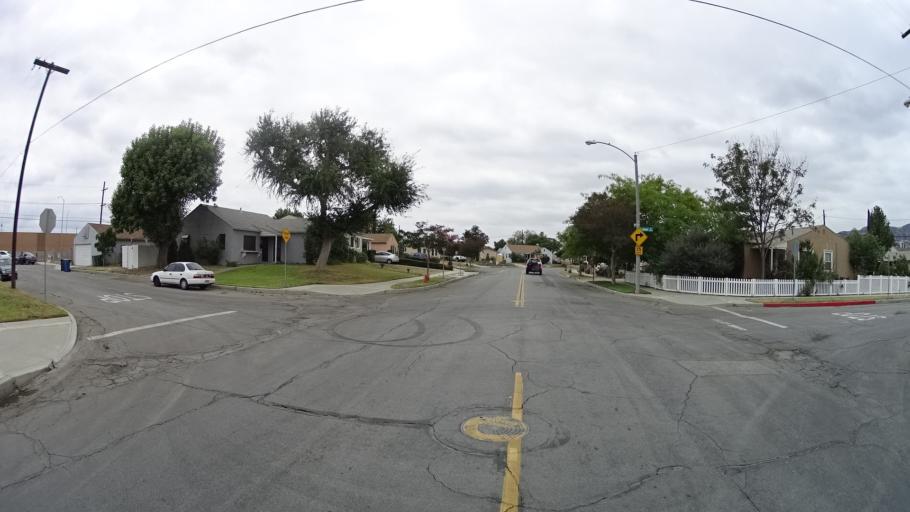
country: US
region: California
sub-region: Los Angeles County
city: Burbank
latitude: 34.1966
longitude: -118.3329
